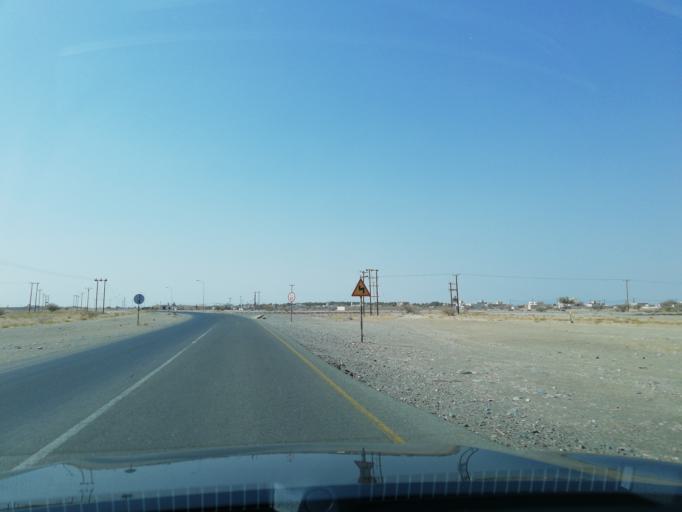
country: OM
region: Muhafazat ad Dakhiliyah
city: Adam
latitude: 22.3130
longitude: 58.0680
